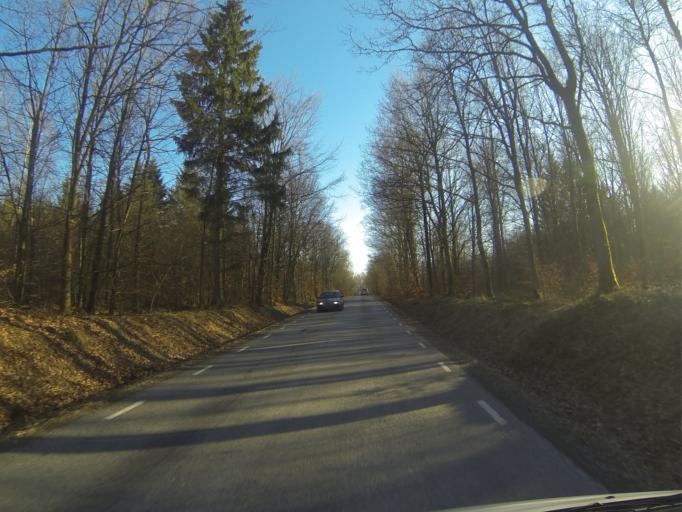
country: SE
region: Skane
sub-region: Horby Kommun
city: Hoerby
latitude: 55.8872
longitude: 13.6650
